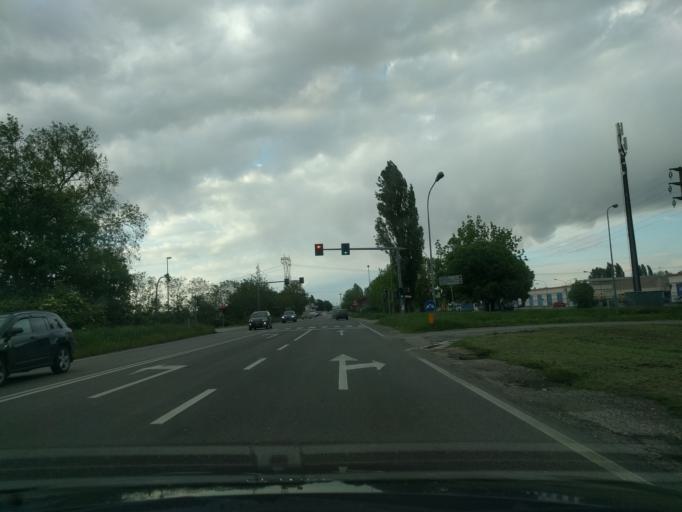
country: IT
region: Emilia-Romagna
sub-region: Provincia di Ferrara
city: Ferrara
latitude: 44.8687
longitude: 11.6015
